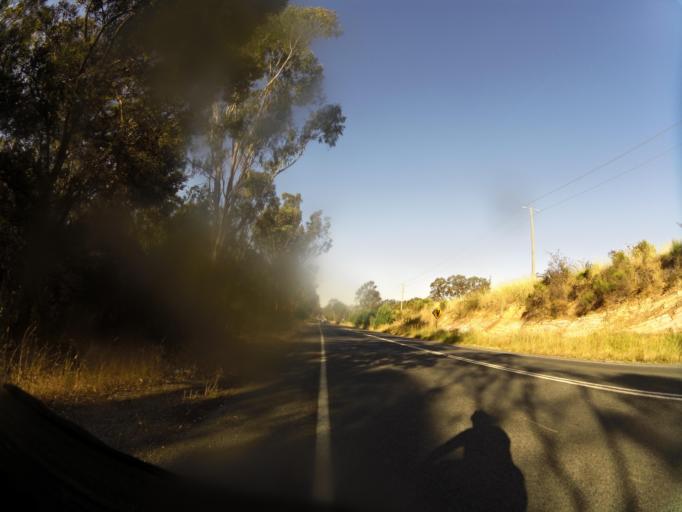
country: AU
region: Victoria
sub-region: Murrindindi
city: Kinglake West
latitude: -37.0287
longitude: 145.1065
